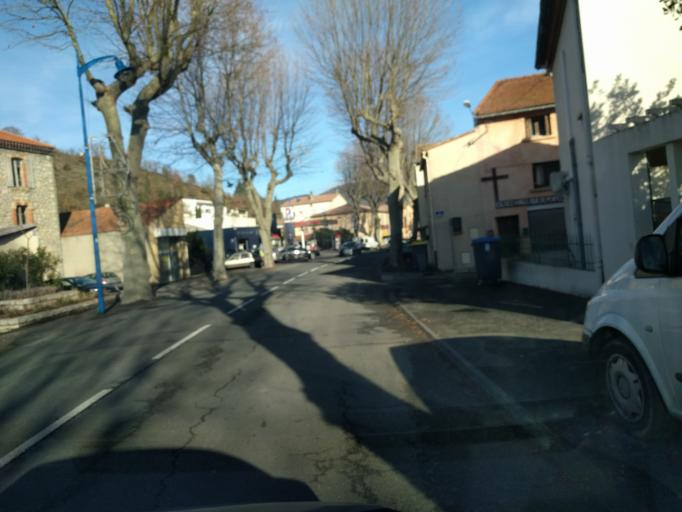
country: FR
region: Languedoc-Roussillon
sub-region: Departement de l'Aude
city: Quillan
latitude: 42.8769
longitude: 2.1828
